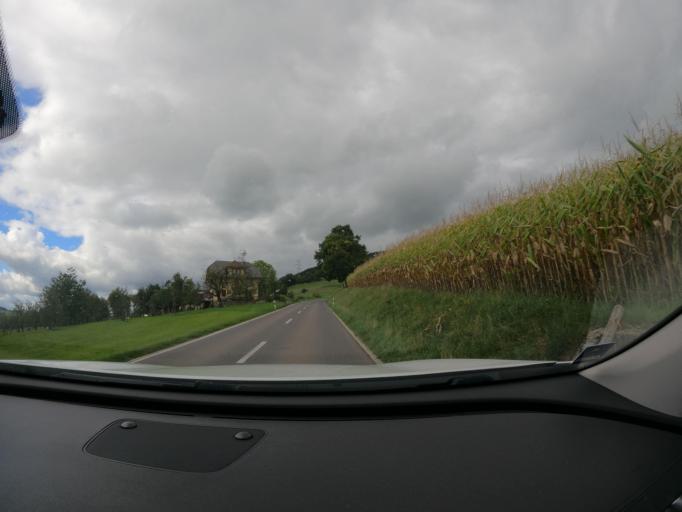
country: CH
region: Lucerne
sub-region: Sursee District
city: Bueron
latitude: 47.2194
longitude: 8.0988
